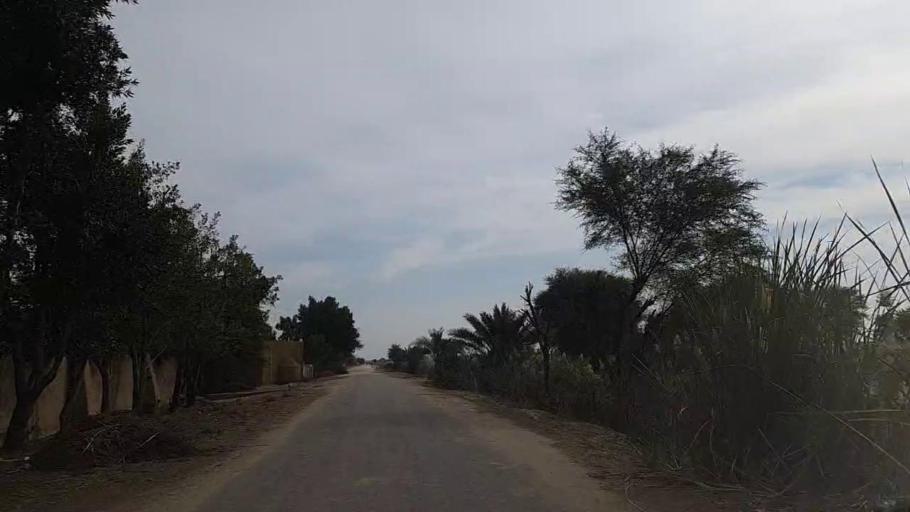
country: PK
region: Sindh
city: Daur
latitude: 26.4160
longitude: 68.4887
